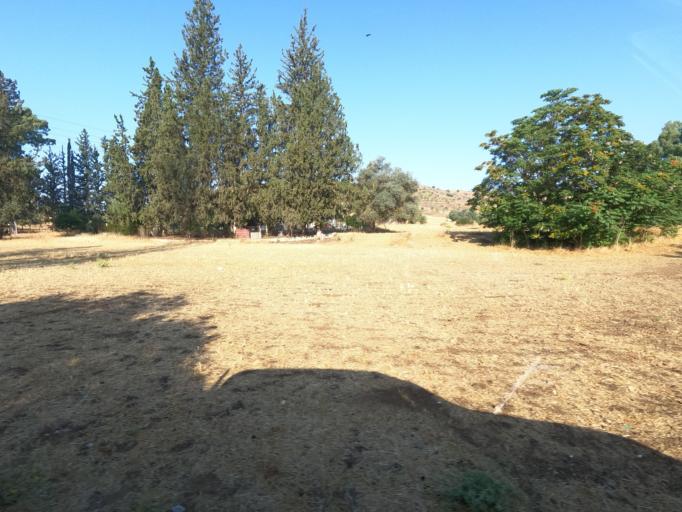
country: CY
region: Lefkosia
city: Lympia
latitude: 34.9868
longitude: 33.4374
